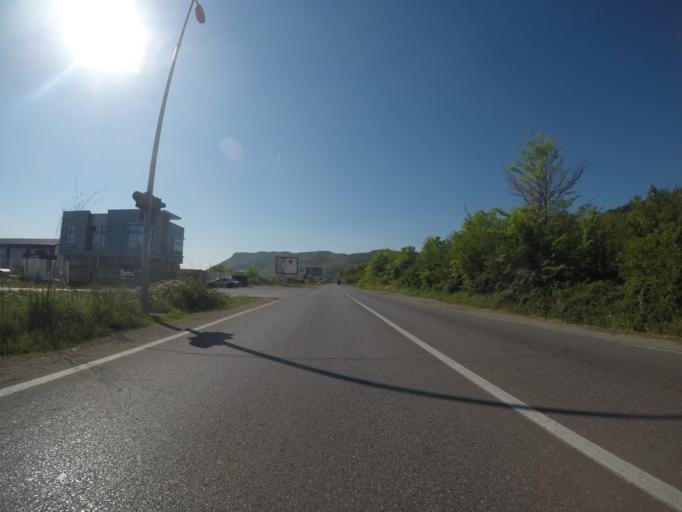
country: ME
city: Spuz
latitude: 42.4717
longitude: 19.1732
